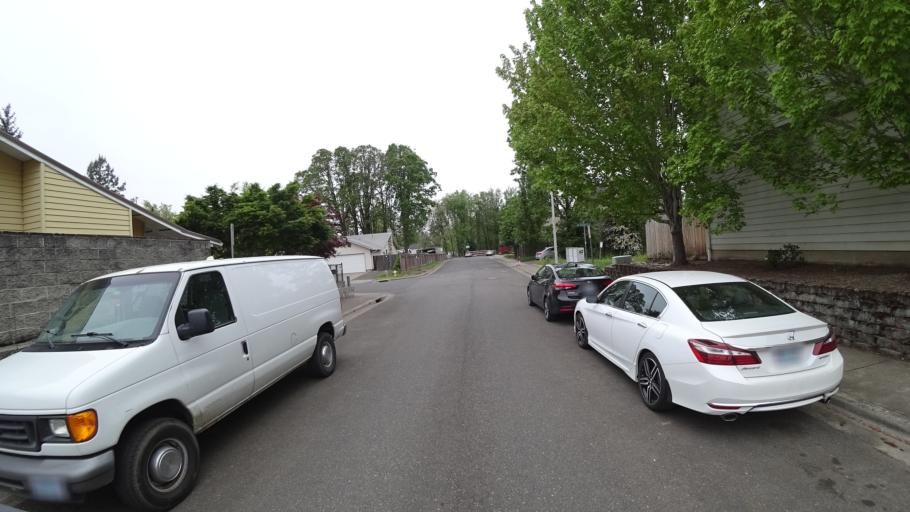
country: US
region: Oregon
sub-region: Washington County
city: Aloha
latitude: 45.5029
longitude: -122.8687
